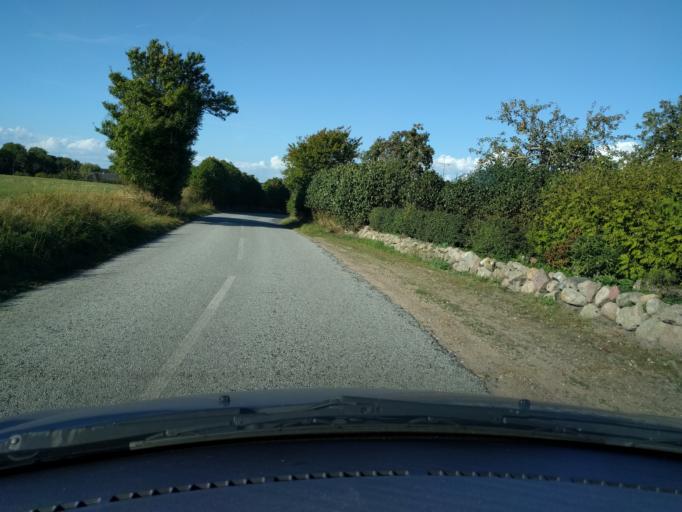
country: DK
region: South Denmark
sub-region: Assens Kommune
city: Harby
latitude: 55.1365
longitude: 10.0267
